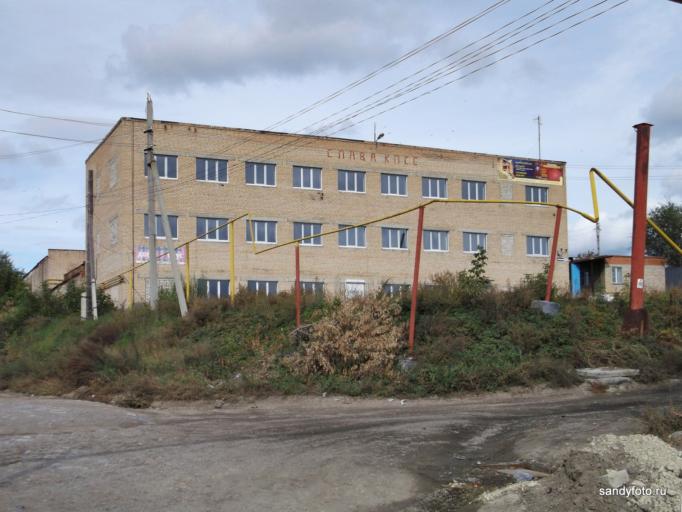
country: RU
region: Chelyabinsk
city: Troitsk
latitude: 54.0997
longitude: 61.5745
